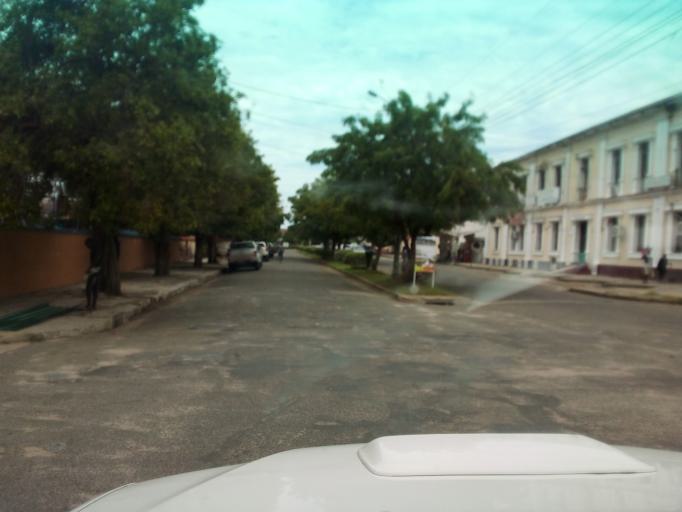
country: MZ
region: Zambezia
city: Quelimane
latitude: -17.8814
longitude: 36.8858
